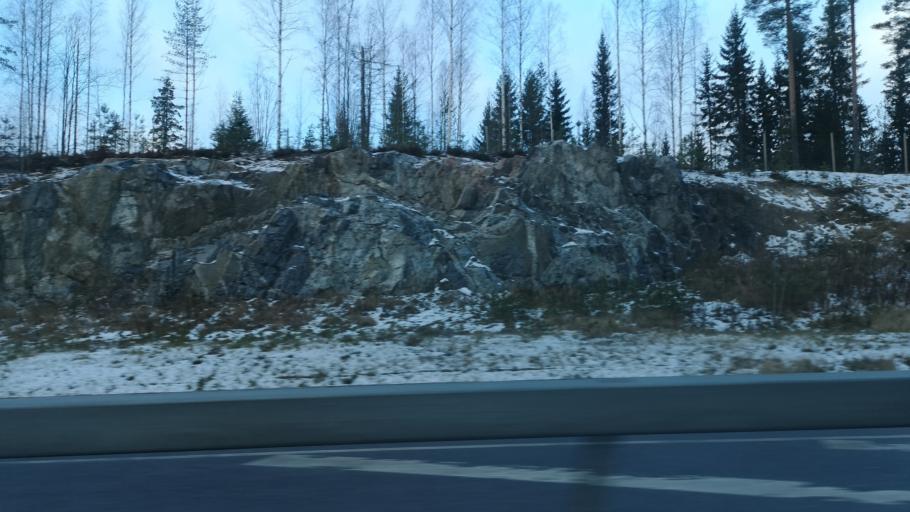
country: FI
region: Southern Savonia
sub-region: Mikkeli
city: Maentyharju
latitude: 61.5042
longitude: 26.7959
